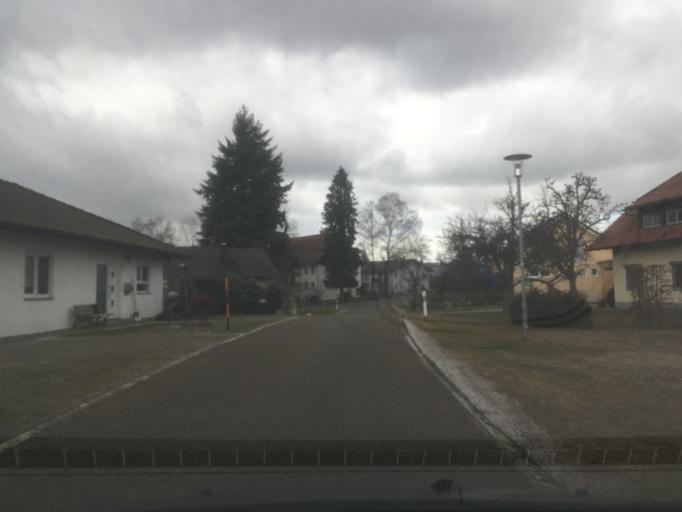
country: DE
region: Baden-Wuerttemberg
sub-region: Freiburg Region
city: Hochenschwand
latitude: 47.6893
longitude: 8.1465
